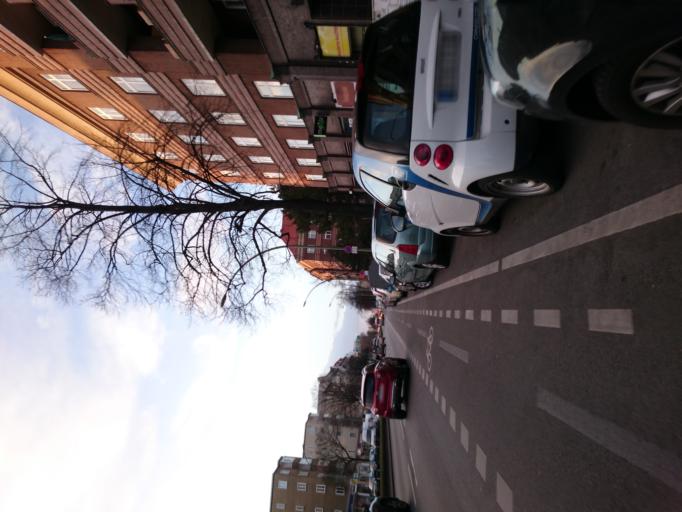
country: DE
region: Berlin
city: Reinickendorf
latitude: 52.5591
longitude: 13.3370
